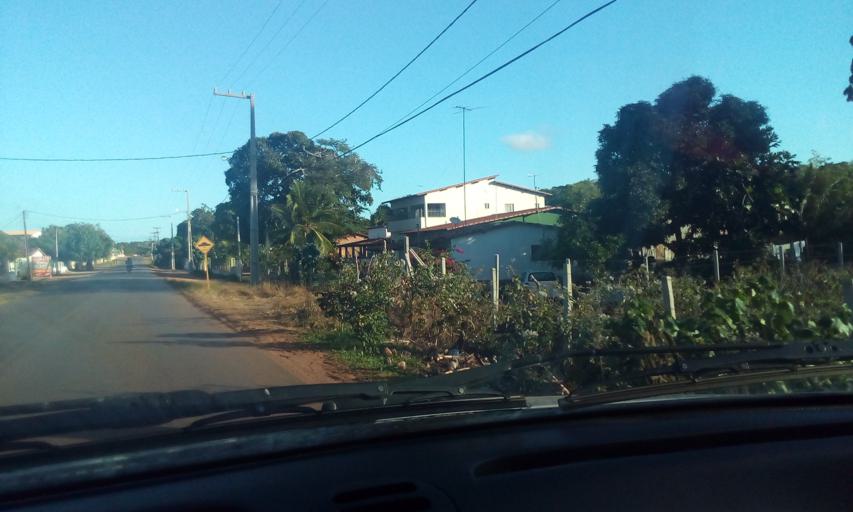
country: BR
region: Rio Grande do Norte
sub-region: Parnamirim
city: Parnamirim
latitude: -5.9528
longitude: -35.1751
